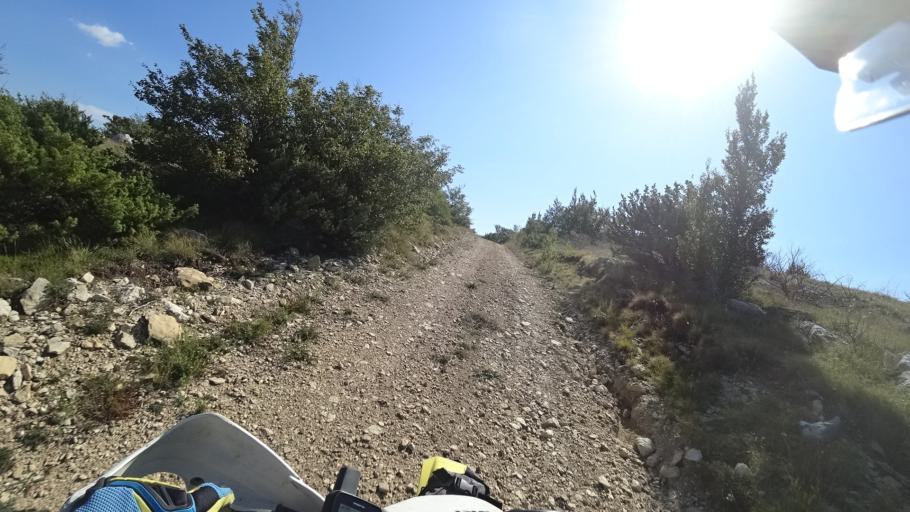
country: HR
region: Sibensko-Kniniska
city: Drnis
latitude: 43.9311
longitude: 16.1638
